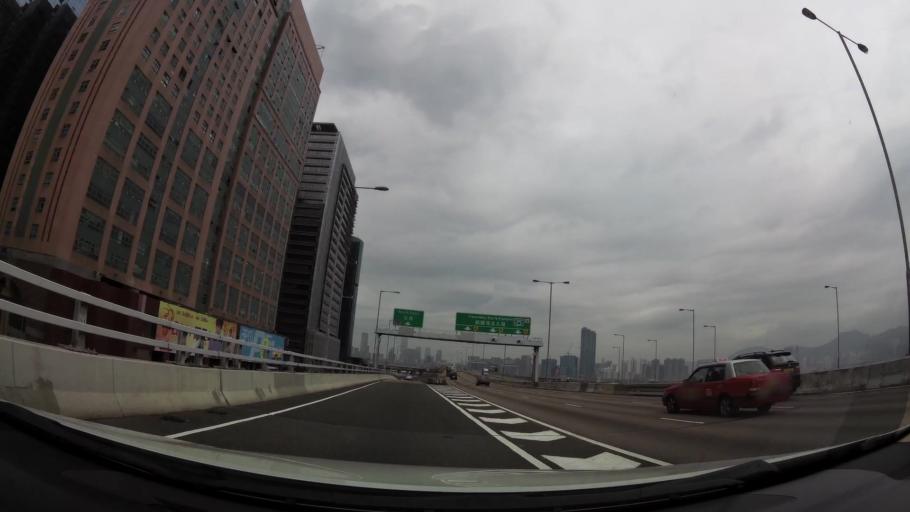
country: HK
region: Kowloon City
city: Kowloon
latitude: 22.2931
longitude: 114.2077
